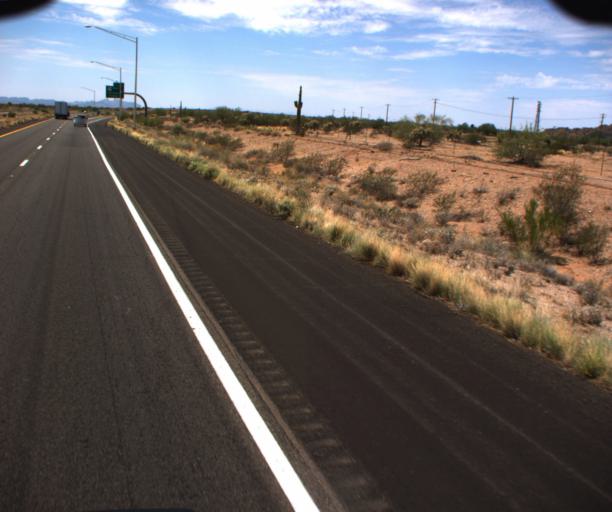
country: US
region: Arizona
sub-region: Pinal County
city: Gold Camp
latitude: 33.2567
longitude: -111.3275
